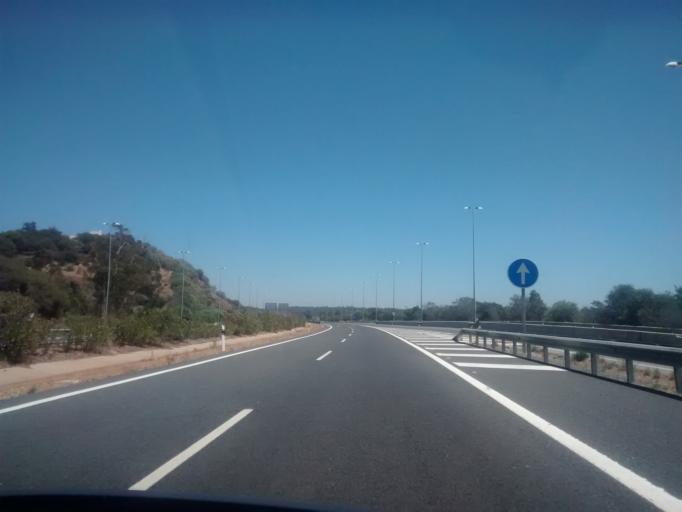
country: ES
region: Andalusia
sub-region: Provincia de Huelva
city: Ayamonte
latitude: 37.2385
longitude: -7.4017
